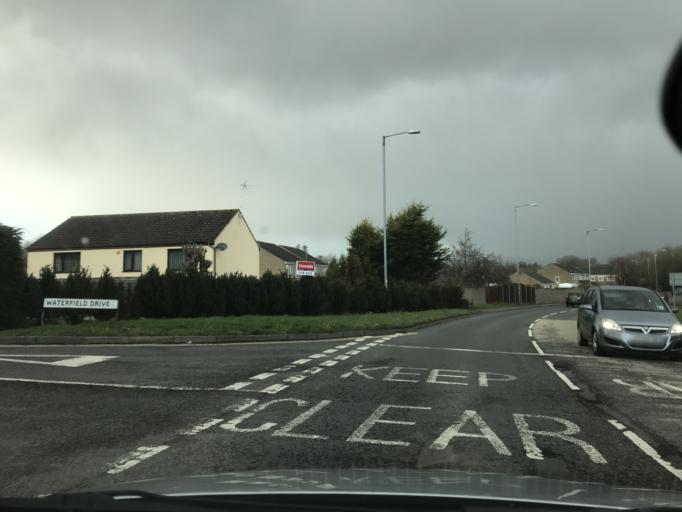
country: GB
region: England
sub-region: Somerset
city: Taunton
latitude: 51.0122
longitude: -3.1316
